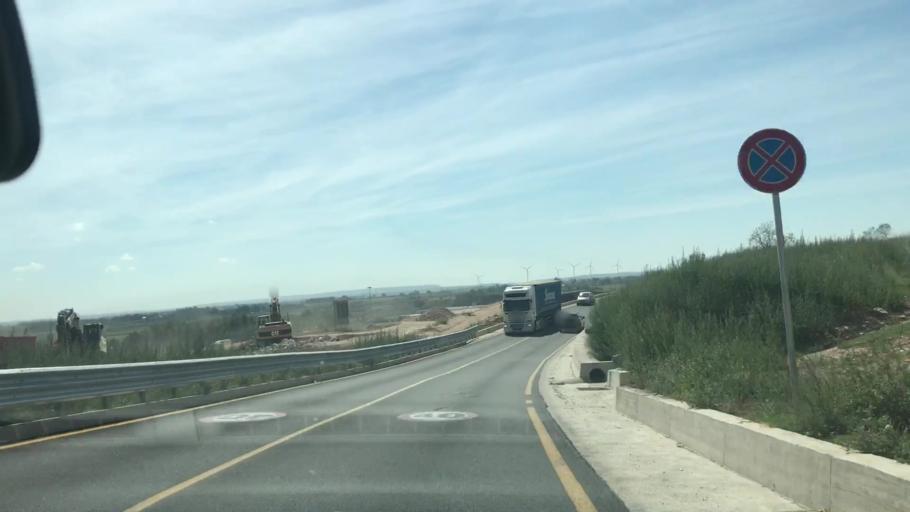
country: IT
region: Apulia
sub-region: Provincia di Bari
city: Altamura
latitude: 40.8100
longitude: 16.5555
